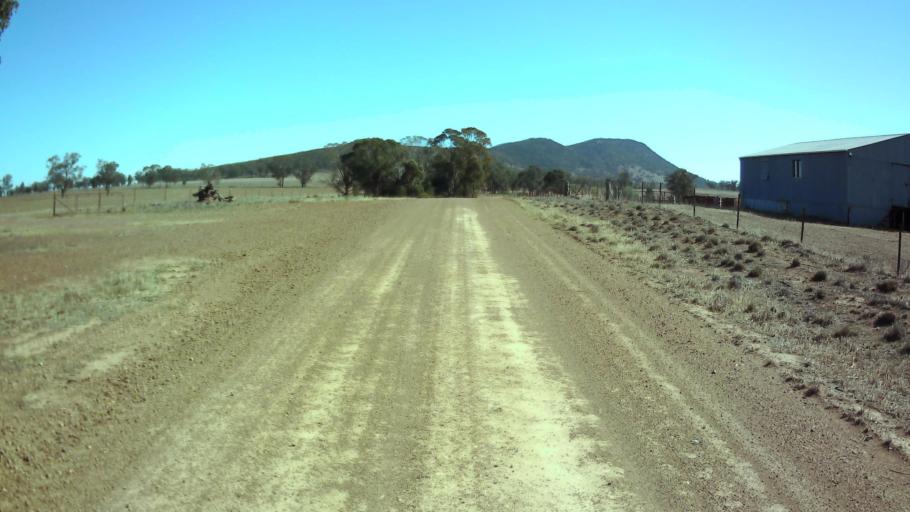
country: AU
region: New South Wales
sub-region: Weddin
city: Grenfell
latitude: -33.7686
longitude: 147.9234
